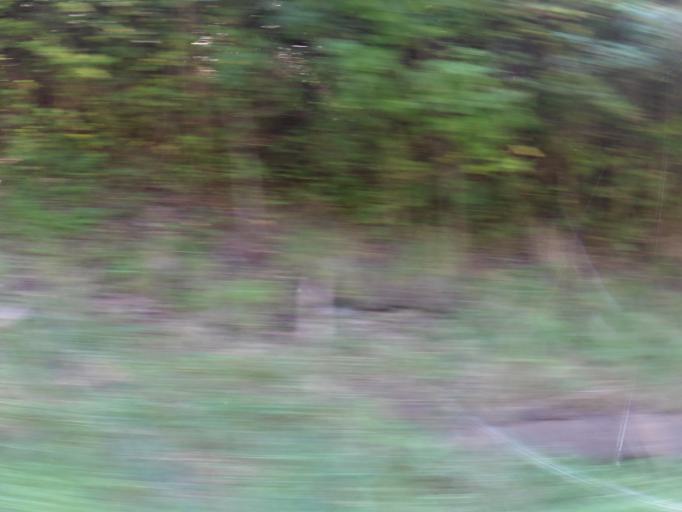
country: US
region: Kentucky
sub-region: Leslie County
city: Hyden
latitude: 37.1409
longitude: -83.3791
